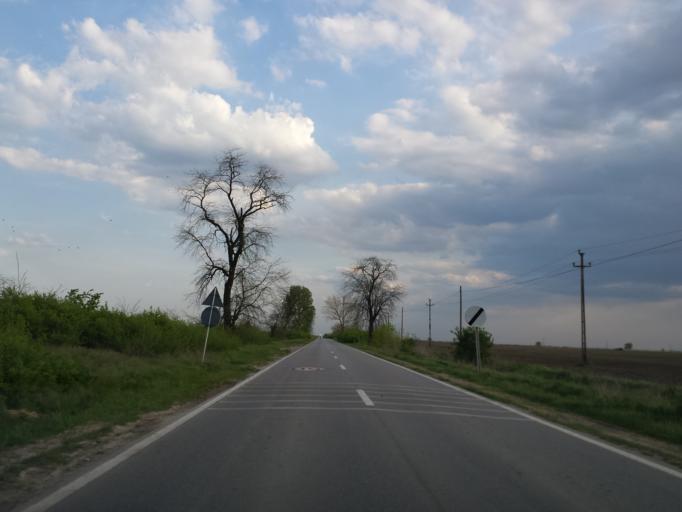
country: RO
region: Timis
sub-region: Comuna Cenad
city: Cenad
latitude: 46.1108
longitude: 20.5955
